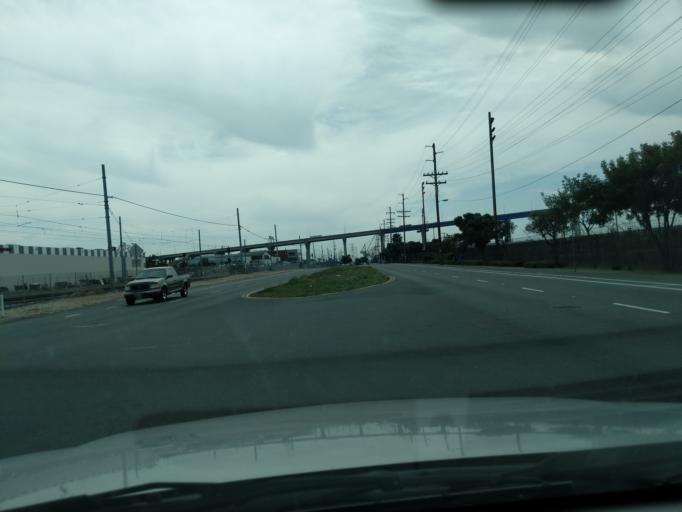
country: US
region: California
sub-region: San Diego County
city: San Diego
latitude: 32.7006
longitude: -117.1509
